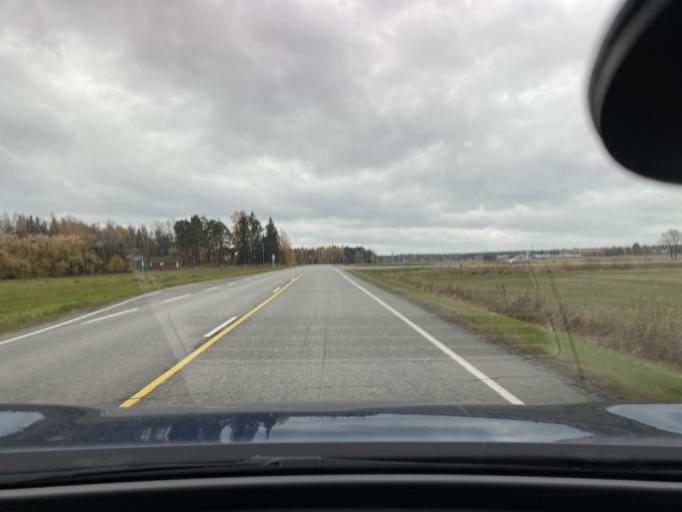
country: FI
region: Satakunta
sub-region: Rauma
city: Kiukainen
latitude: 61.1867
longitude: 22.0605
